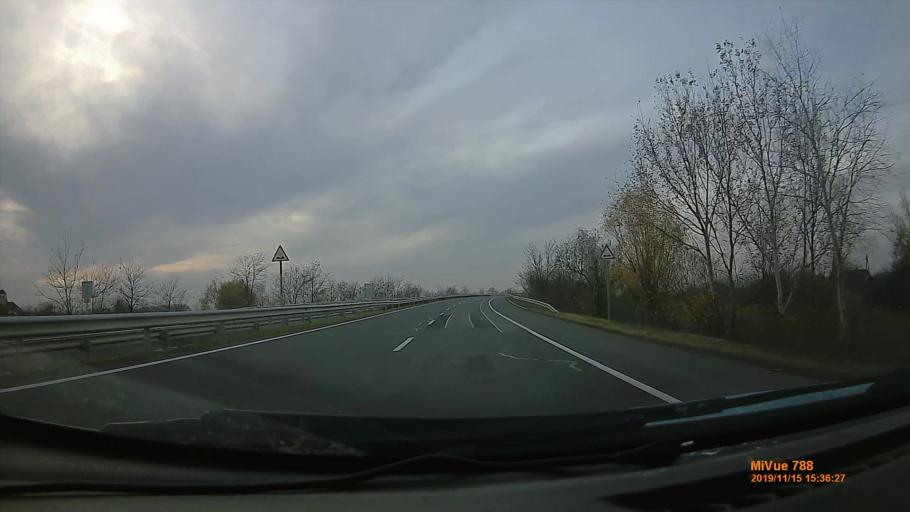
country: HU
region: Bekes
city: Gyula
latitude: 46.6572
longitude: 21.2128
